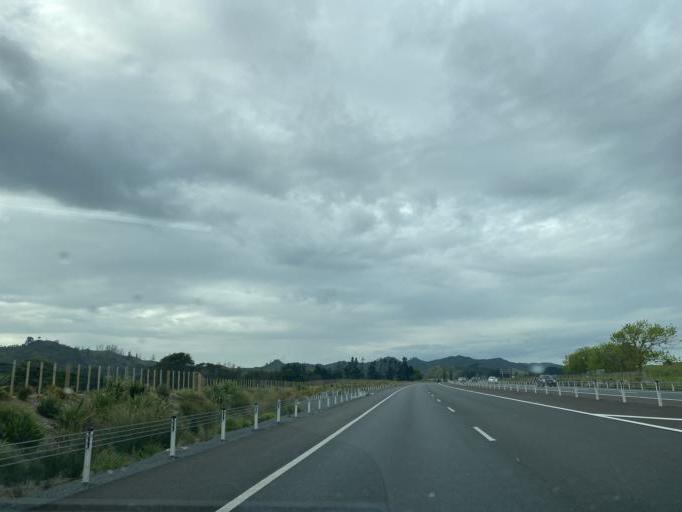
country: NZ
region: Waikato
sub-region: Waikato District
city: Ngaruawahia
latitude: -37.6111
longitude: 175.2047
